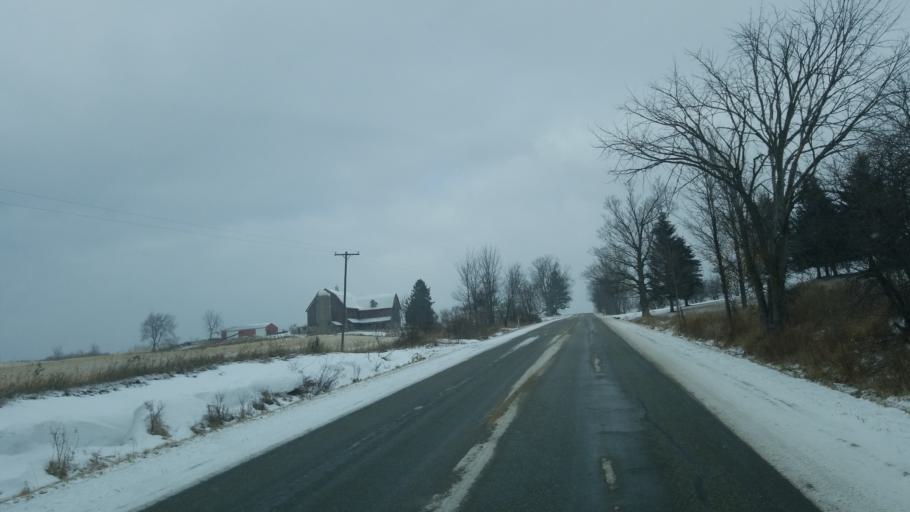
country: US
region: Michigan
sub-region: Osceola County
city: Evart
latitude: 43.9402
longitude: -85.2467
